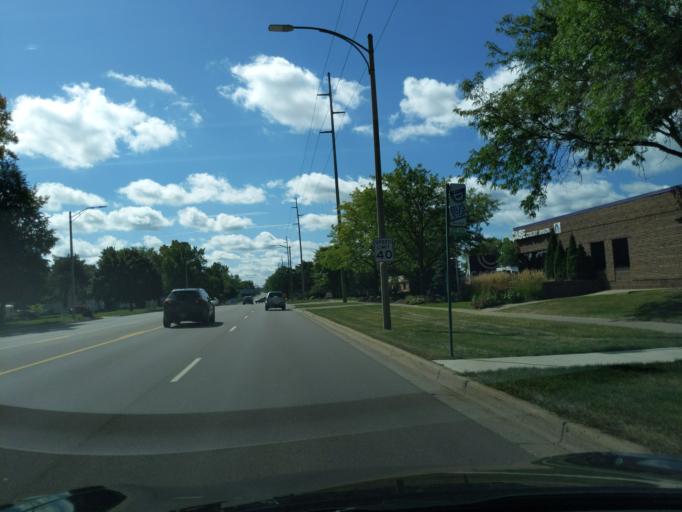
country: US
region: Michigan
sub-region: Ingham County
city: Lansing
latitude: 42.6895
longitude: -84.5382
